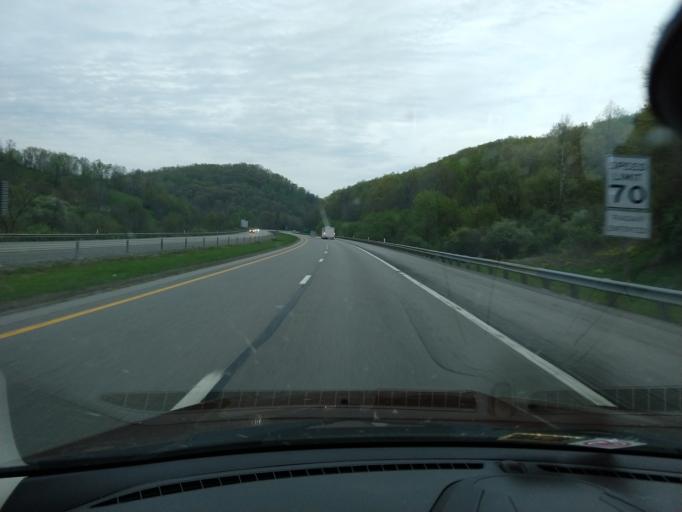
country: US
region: West Virginia
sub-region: Lewis County
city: Weston
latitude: 38.9729
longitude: -80.5112
